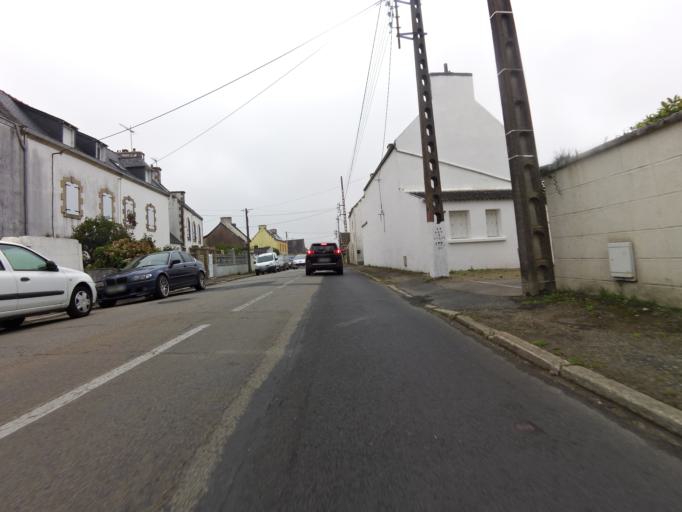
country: FR
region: Brittany
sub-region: Departement du Finistere
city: Audierne
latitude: 48.0168
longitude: -4.5173
